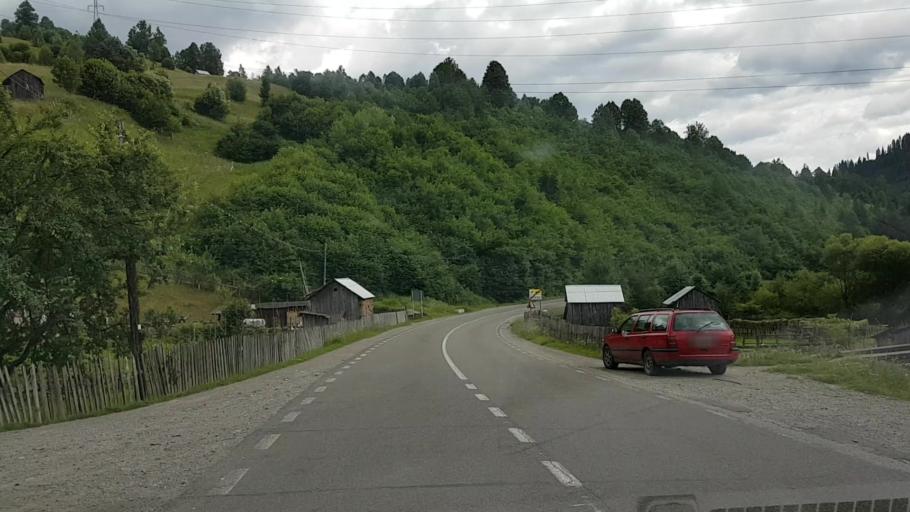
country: RO
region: Suceava
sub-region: Comuna Brosteni
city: Brosteni
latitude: 47.2358
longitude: 25.7418
